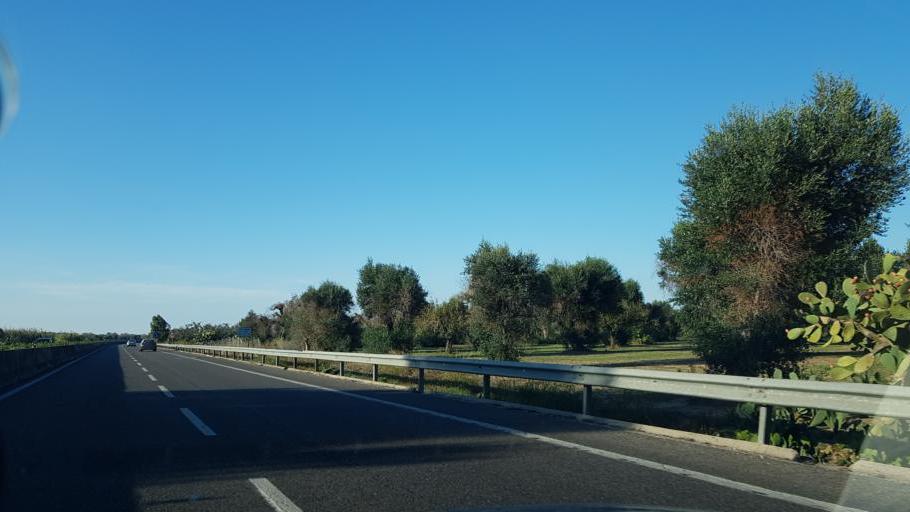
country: IT
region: Apulia
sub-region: Provincia di Brindisi
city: San Pietro Vernotico
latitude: 40.5210
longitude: 18.0170
